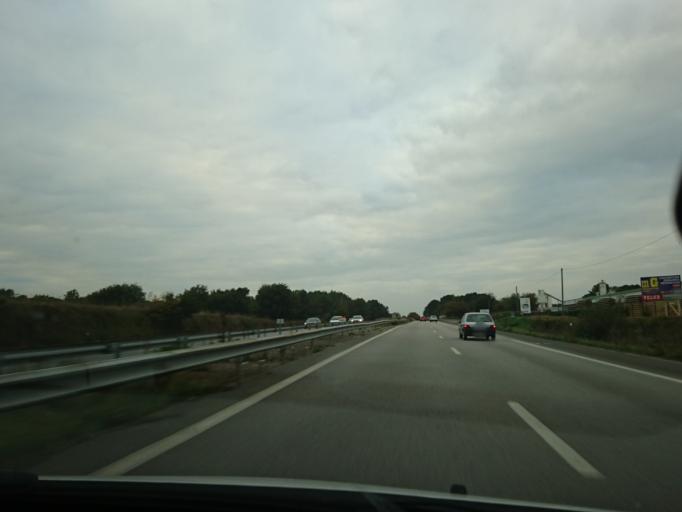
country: FR
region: Brittany
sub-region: Departement du Morbihan
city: Landaul
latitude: 47.7318
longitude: -3.0912
